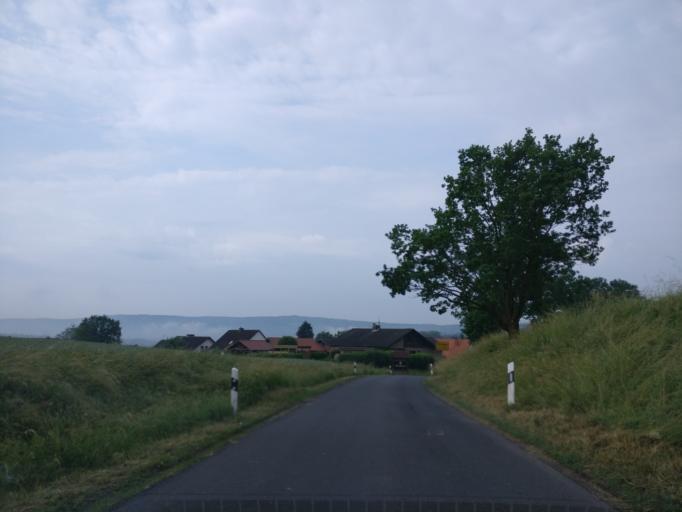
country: DE
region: Lower Saxony
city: Scheden
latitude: 51.4283
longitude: 9.7162
